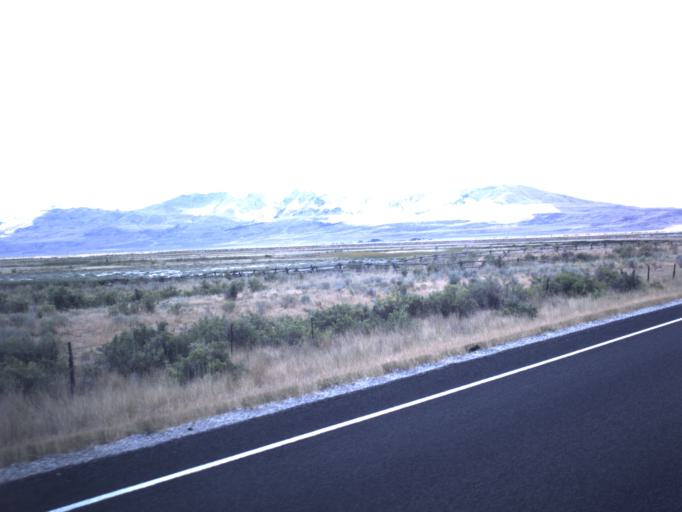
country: US
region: Utah
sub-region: Box Elder County
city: Tremonton
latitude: 41.6295
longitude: -112.4137
